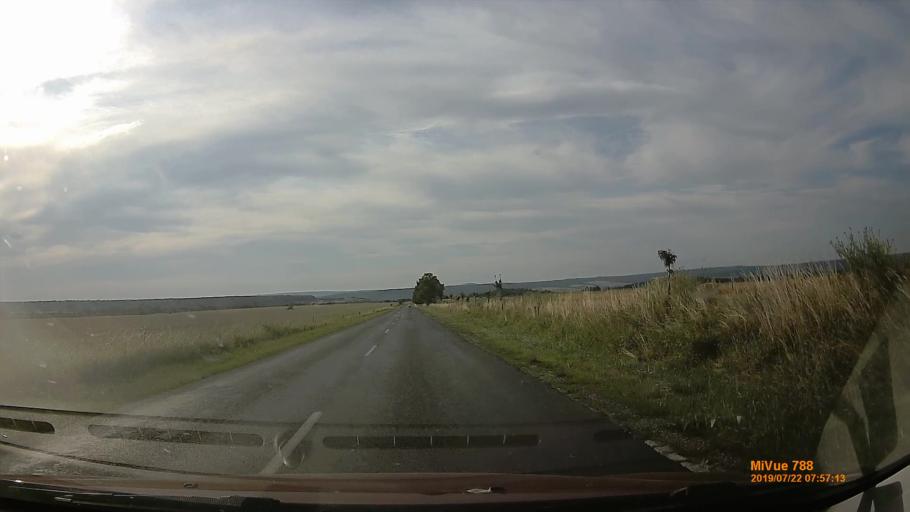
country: HU
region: Veszprem
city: Ajka
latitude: 47.0190
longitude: 17.5803
